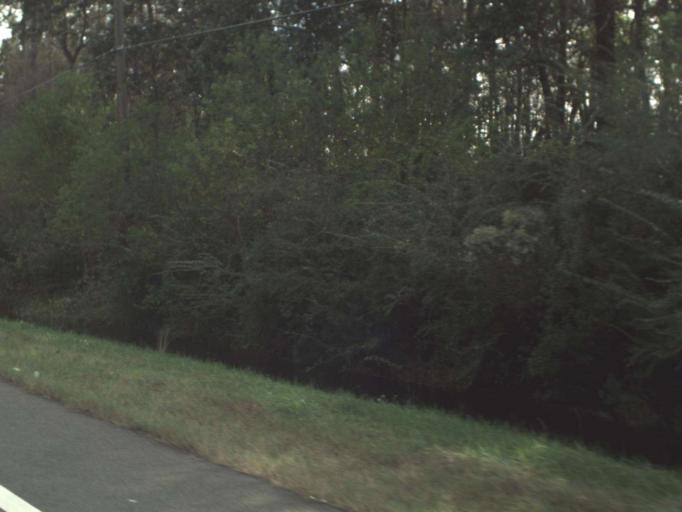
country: US
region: Florida
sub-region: Escambia County
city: Myrtle Grove
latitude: 30.3912
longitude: -87.3104
